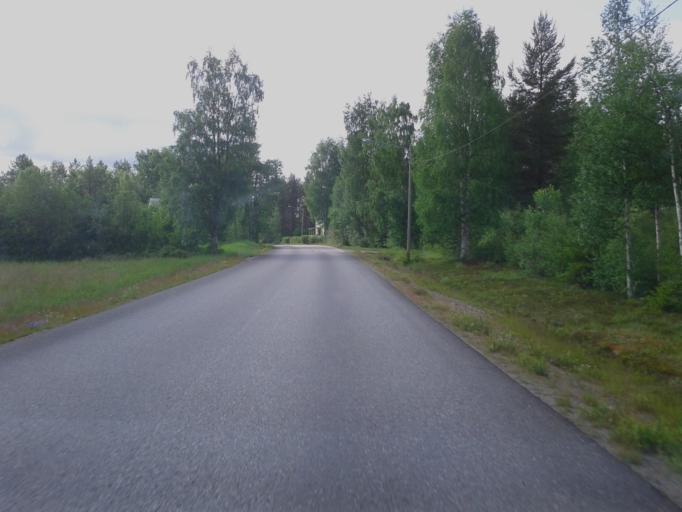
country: SE
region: Vaesterbotten
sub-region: Sorsele Kommun
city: Sorsele
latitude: 65.2795
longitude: 17.9326
